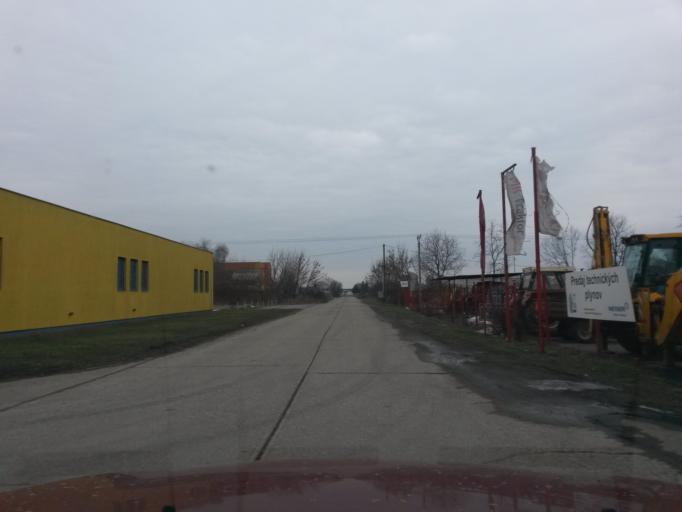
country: SK
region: Kosicky
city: Michalovce
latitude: 48.7514
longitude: 21.8863
